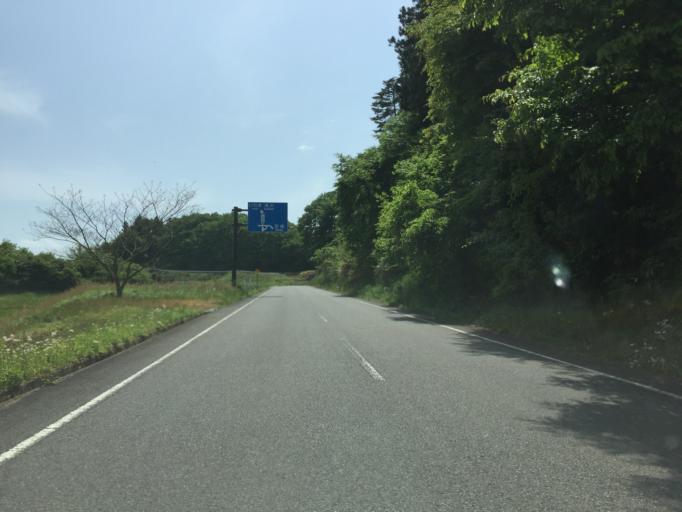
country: JP
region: Fukushima
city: Ishikawa
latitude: 37.1756
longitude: 140.5058
